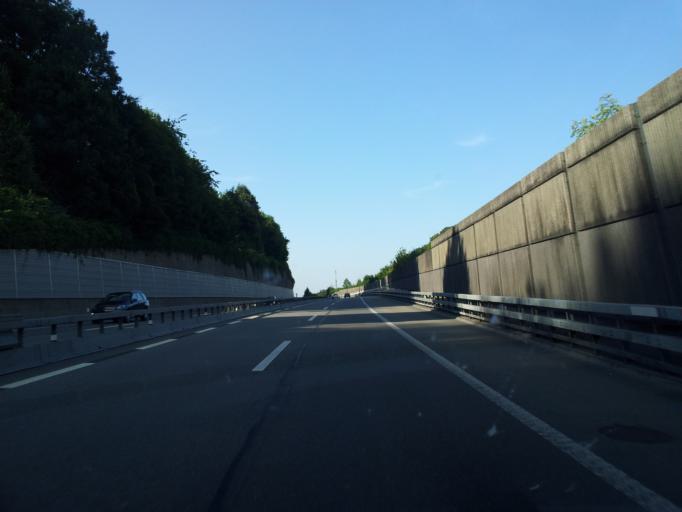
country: CH
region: Fribourg
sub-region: Sense District
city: Flamatt
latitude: 46.8973
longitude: 7.3523
